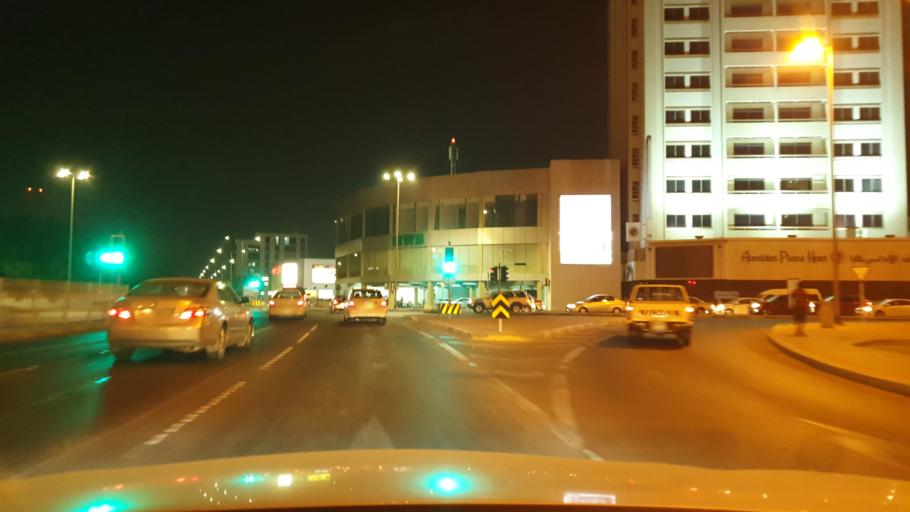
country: BH
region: Manama
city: Manama
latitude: 26.2214
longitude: 50.5847
